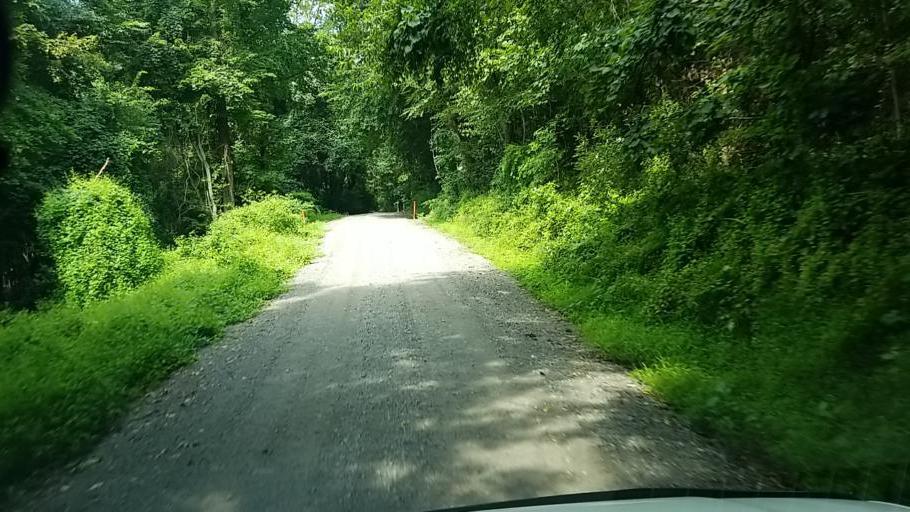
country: US
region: Pennsylvania
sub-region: Dauphin County
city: Millersburg
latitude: 40.5261
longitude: -76.9445
